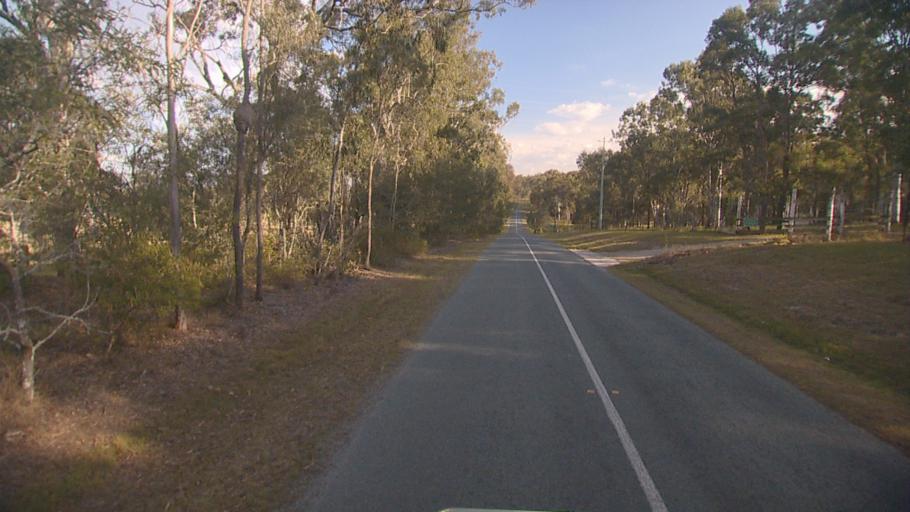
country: AU
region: Queensland
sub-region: Gold Coast
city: Ormeau Hills
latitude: -27.8290
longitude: 153.1723
